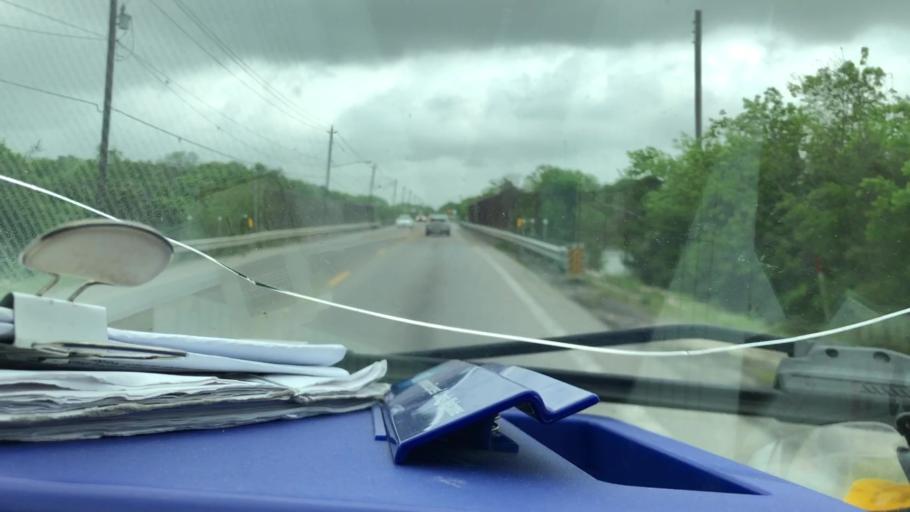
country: US
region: Texas
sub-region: Galveston County
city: Bacliff
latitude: 29.4851
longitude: -94.9689
